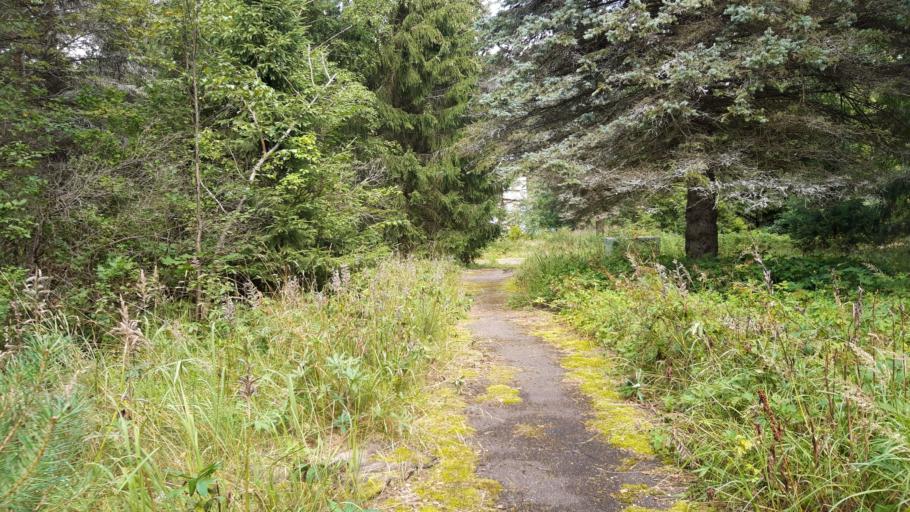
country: RU
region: Tverskaya
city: Konakovo
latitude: 56.6684
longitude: 36.6829
